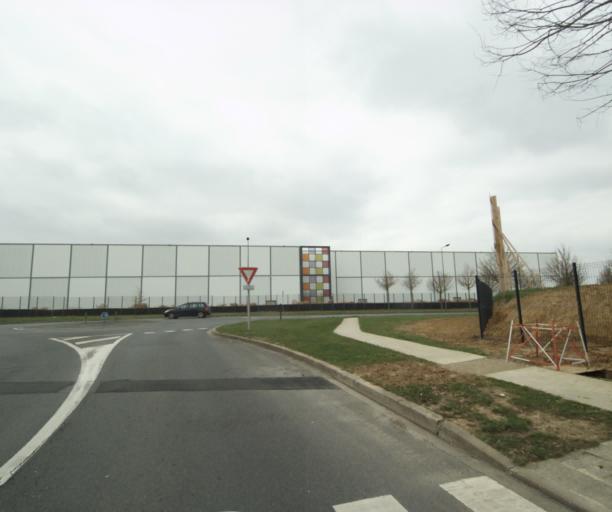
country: FR
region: Ile-de-France
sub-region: Departement du Val-d'Oise
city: Vaureal
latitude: 49.0556
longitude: 2.0331
